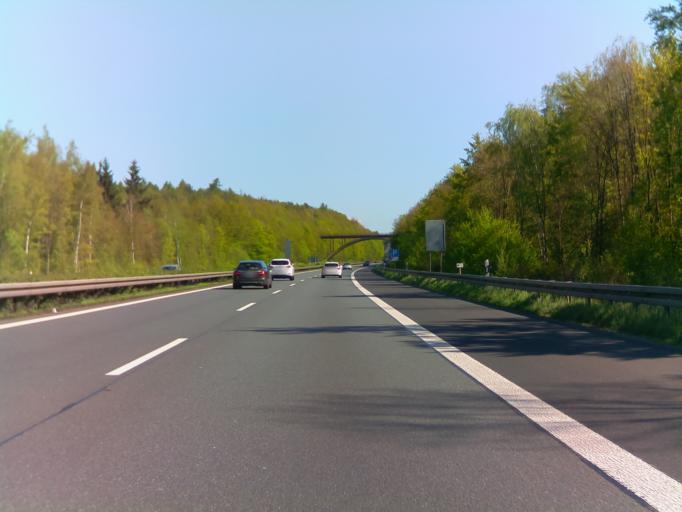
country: DE
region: Bavaria
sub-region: Regierungsbezirk Unterfranken
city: Arnstein
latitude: 49.9185
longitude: 9.9969
